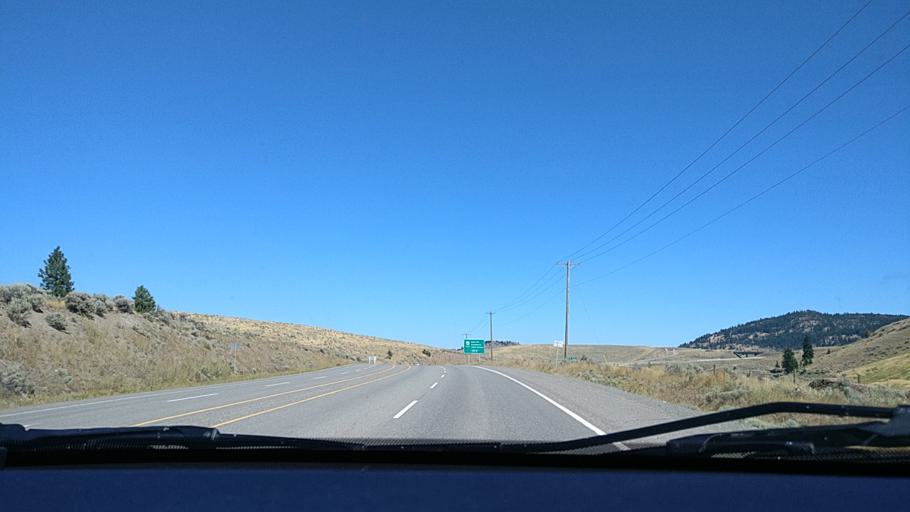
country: CA
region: British Columbia
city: Kamloops
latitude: 50.6687
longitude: -120.4743
